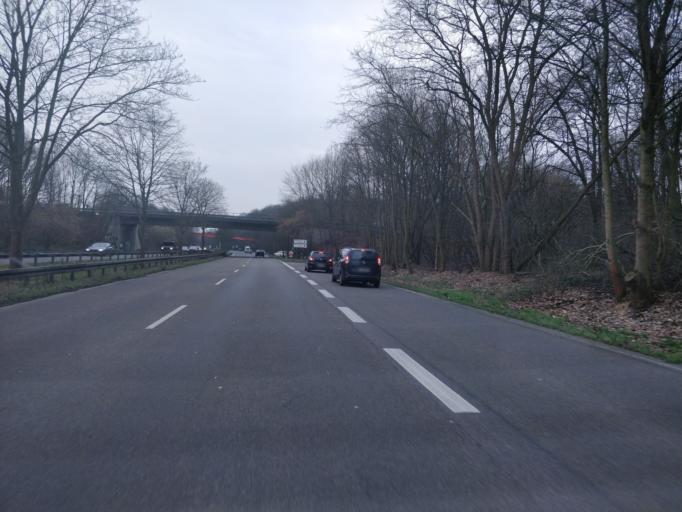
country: DE
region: North Rhine-Westphalia
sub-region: Regierungsbezirk Koln
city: Mengenich
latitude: 50.9528
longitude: 6.8708
